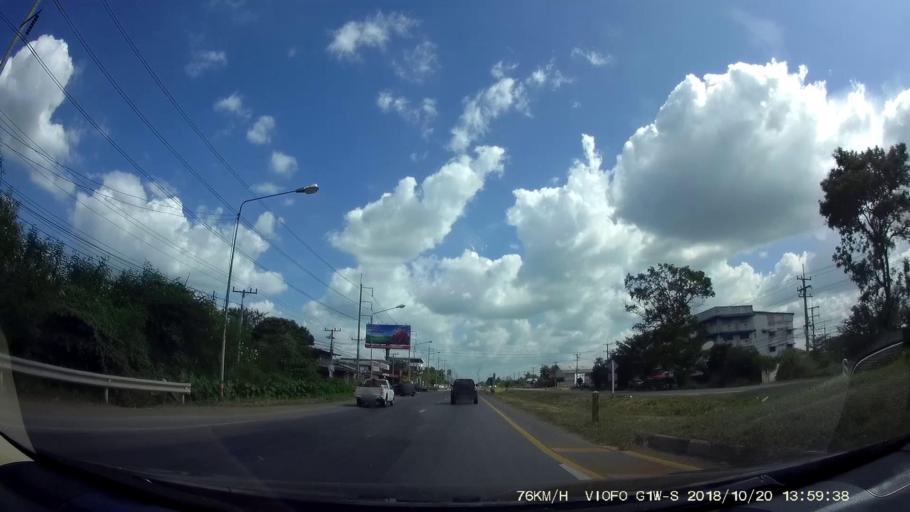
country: TH
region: Khon Kaen
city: Chum Phae
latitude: 16.5227
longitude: 102.1140
